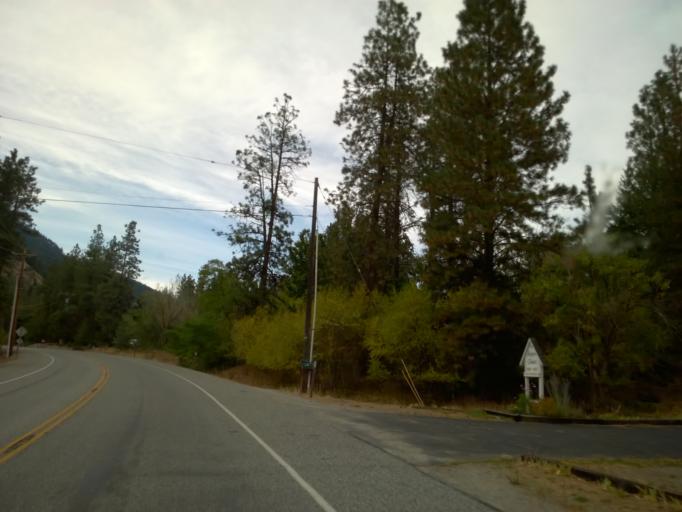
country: US
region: Washington
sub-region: Chelan County
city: Leavenworth
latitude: 47.5826
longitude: -120.6729
